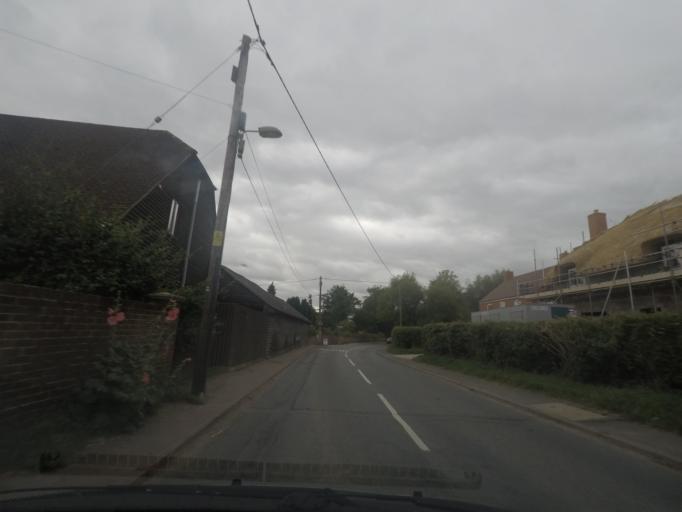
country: GB
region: England
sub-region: Oxfordshire
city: Harwell
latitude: 51.6259
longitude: -1.3007
